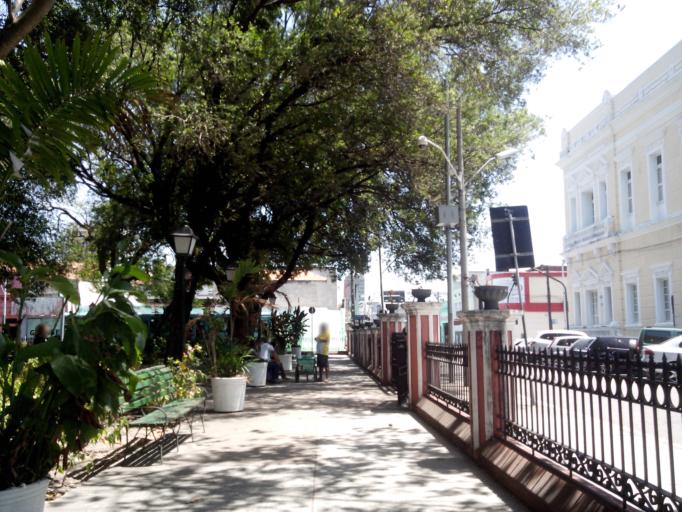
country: BR
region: Ceara
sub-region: Fortaleza
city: Fortaleza
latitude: -3.7223
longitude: -38.5268
